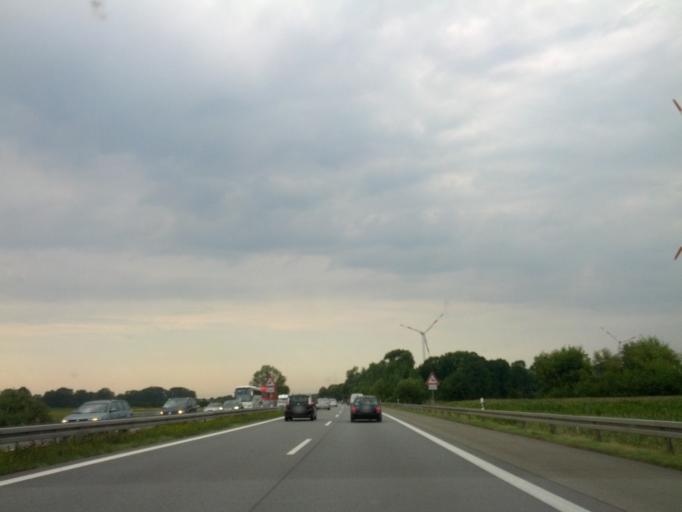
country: DE
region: Brandenburg
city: Walsleben
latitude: 52.9338
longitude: 12.6978
